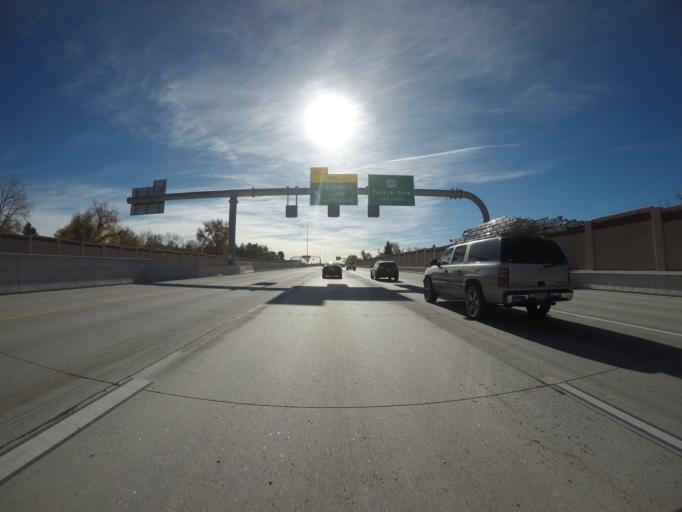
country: US
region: Colorado
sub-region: Adams County
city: Westminster
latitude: 39.8464
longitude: -105.0442
